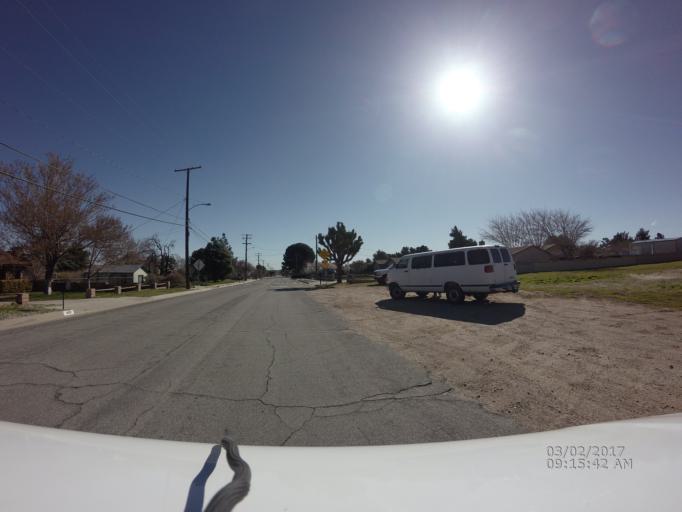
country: US
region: California
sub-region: Los Angeles County
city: Quartz Hill
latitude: 34.6346
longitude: -118.2179
